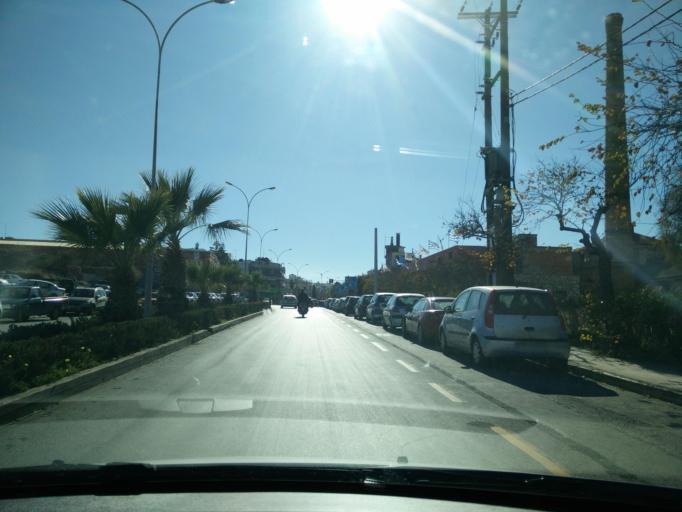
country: GR
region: Crete
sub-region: Nomos Irakleiou
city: Irakleion
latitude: 35.3401
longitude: 25.1421
